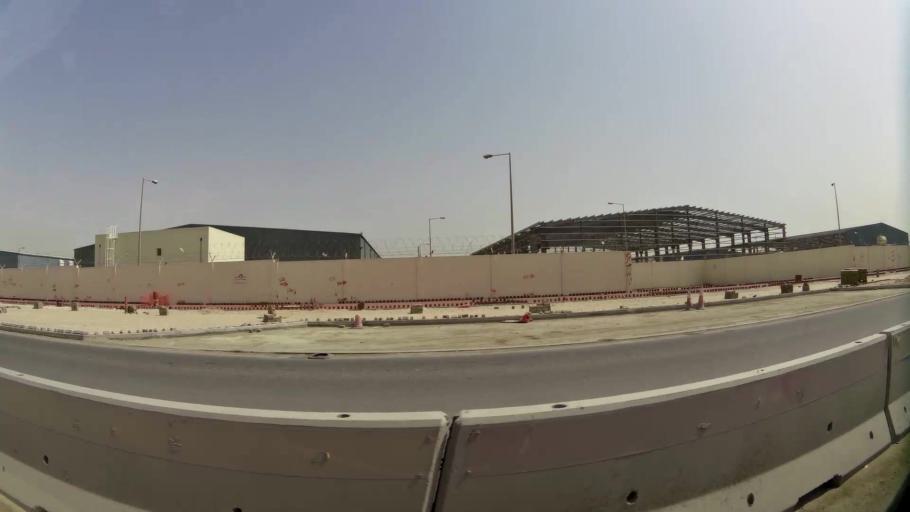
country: QA
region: Baladiyat ar Rayyan
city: Ar Rayyan
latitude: 25.2023
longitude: 51.4123
